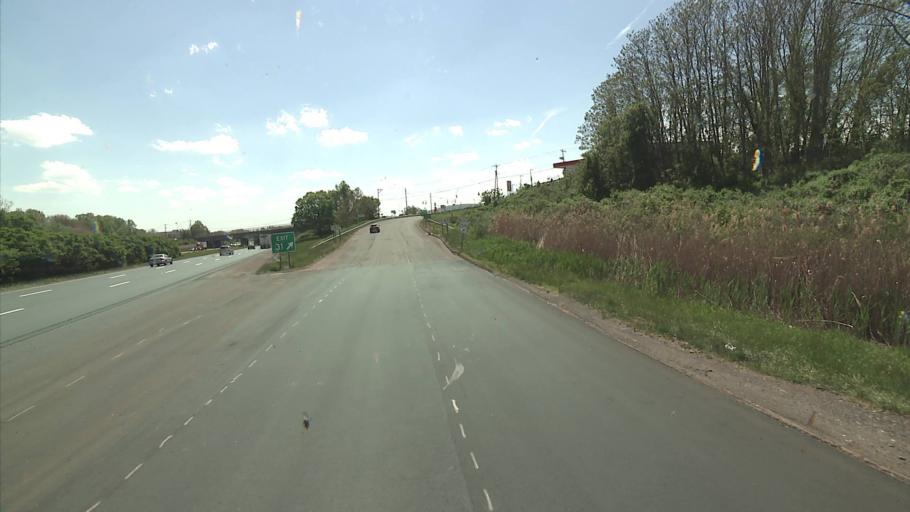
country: US
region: Connecticut
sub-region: Hartford County
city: Plainville
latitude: 41.6147
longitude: -72.8975
